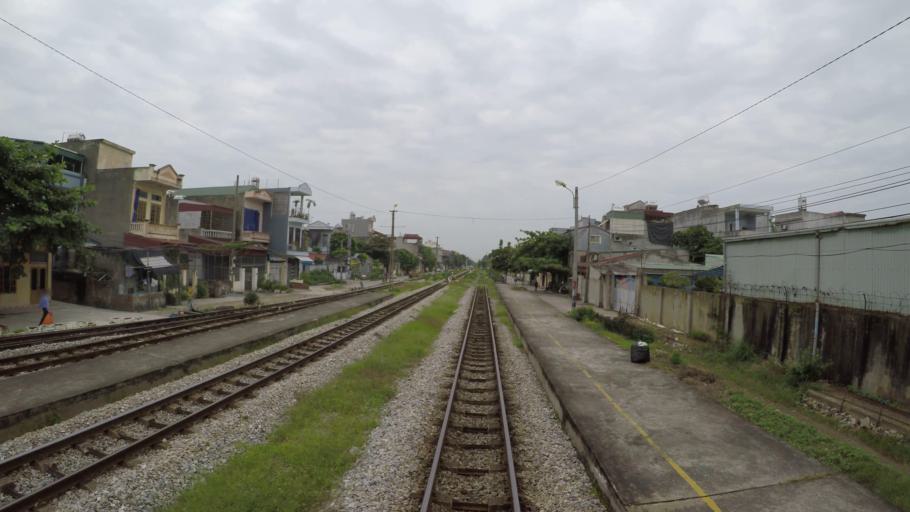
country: VN
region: Hai Duong
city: Thanh Pho Hai Duong
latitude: 20.9482
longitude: 106.3212
